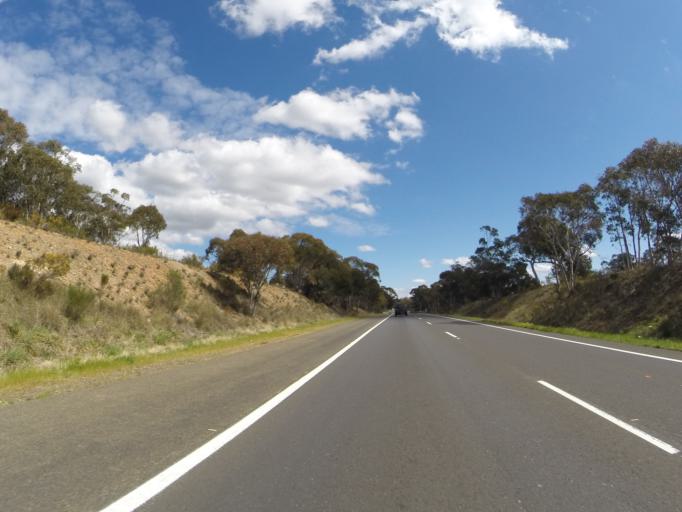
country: AU
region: New South Wales
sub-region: Goulburn Mulwaree
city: Goulburn
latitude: -34.7448
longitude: 149.8809
